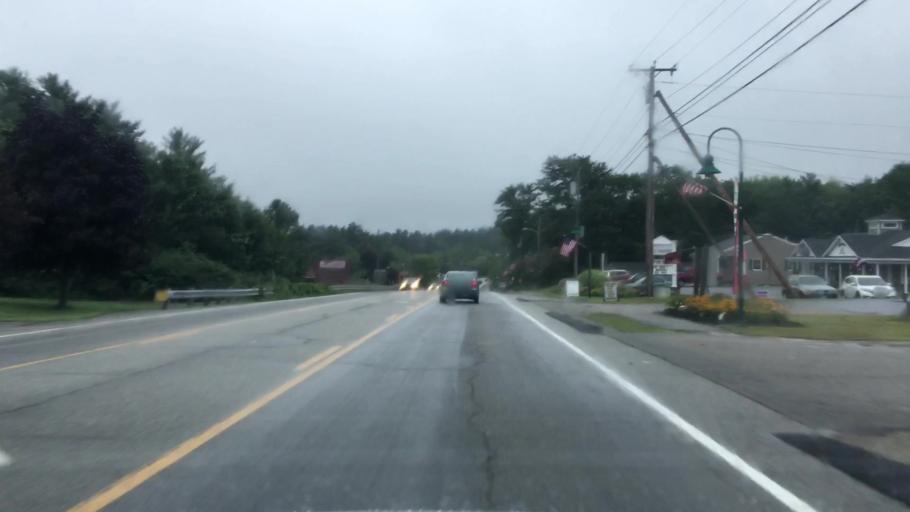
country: US
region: Maine
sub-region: Cumberland County
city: Raymond
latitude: 43.8842
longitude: -70.4651
